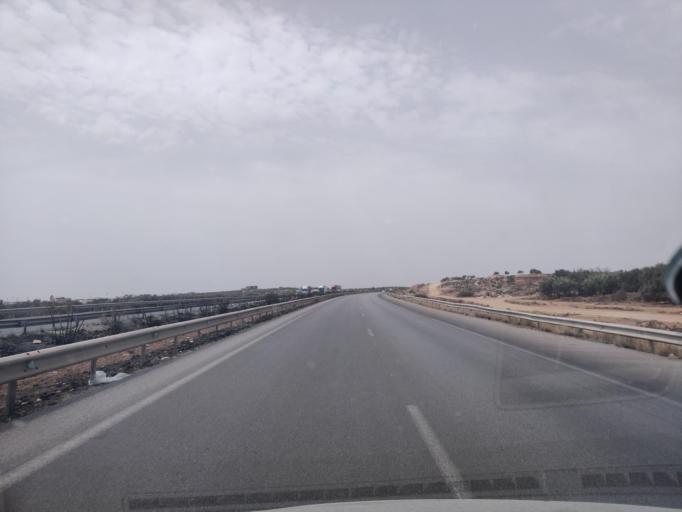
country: TN
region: Susah
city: Sidi Bou Ali
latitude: 35.9610
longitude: 10.4857
